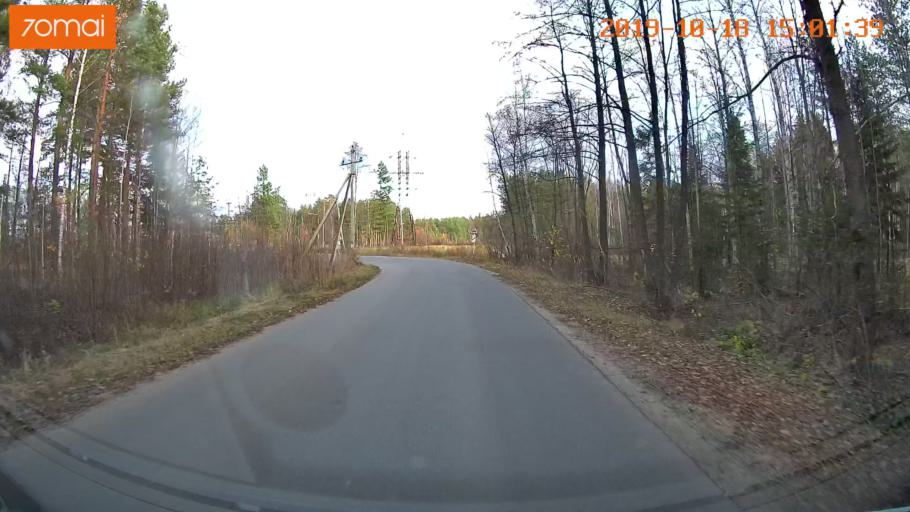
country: RU
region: Vladimir
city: Gus'-Khrustal'nyy
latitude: 55.5003
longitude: 40.6073
